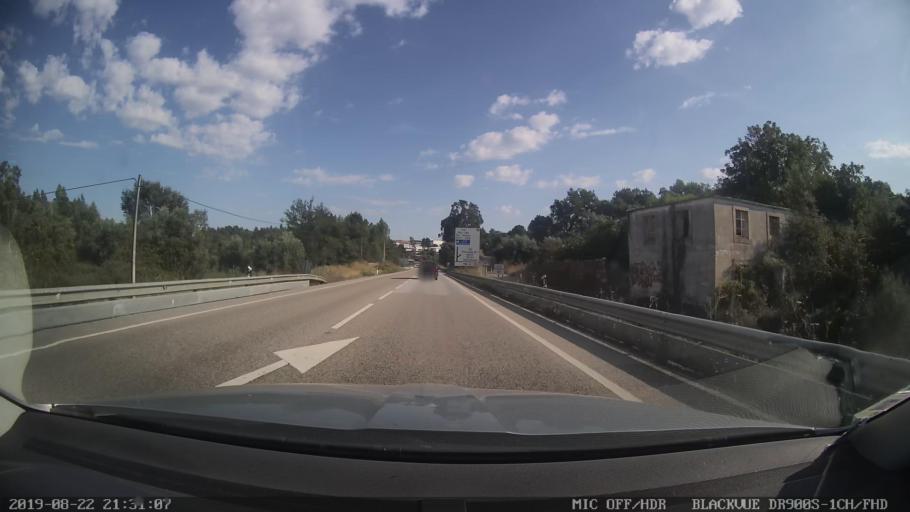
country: PT
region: Leiria
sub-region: Pedrogao Grande
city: Pedrogao Grande
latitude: 39.9165
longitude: -8.1537
